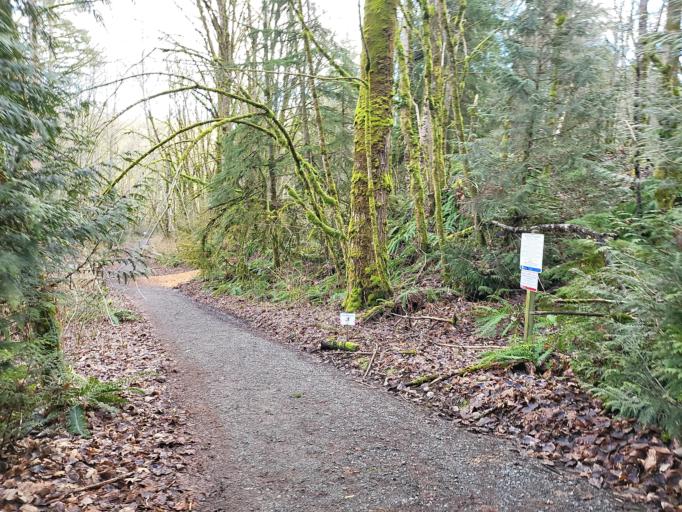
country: US
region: Washington
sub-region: King County
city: Newcastle
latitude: 47.5335
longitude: -122.1305
